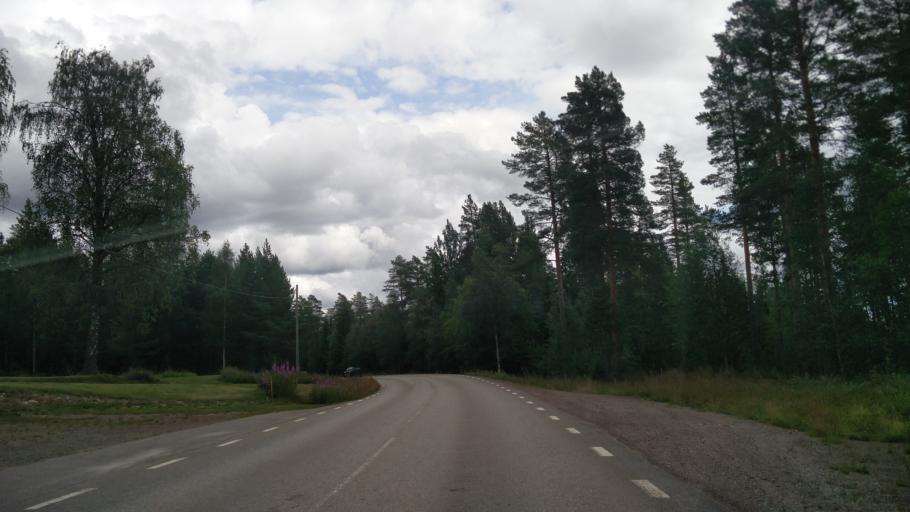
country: NO
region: Hedmark
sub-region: Trysil
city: Innbygda
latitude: 61.1757
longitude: 12.8662
